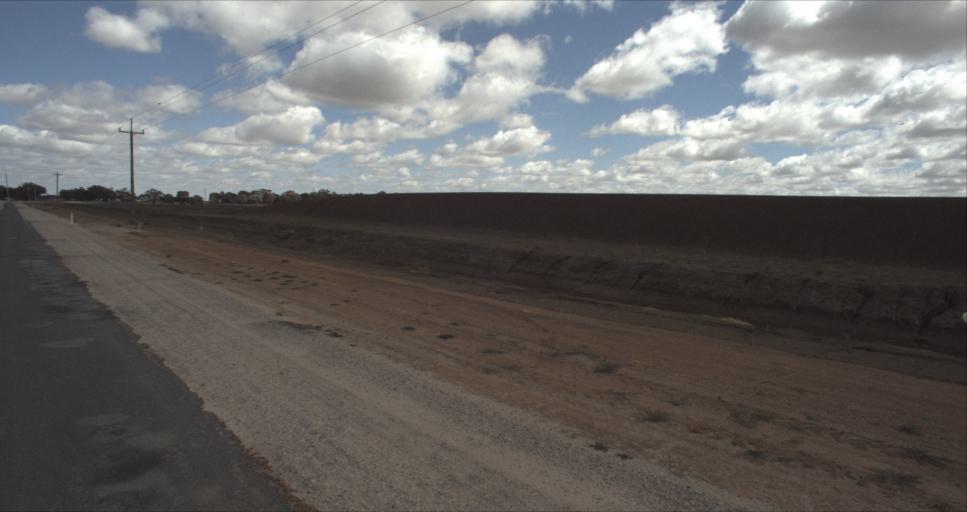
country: AU
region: New South Wales
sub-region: Murrumbidgee Shire
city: Darlington Point
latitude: -34.5752
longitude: 146.1714
